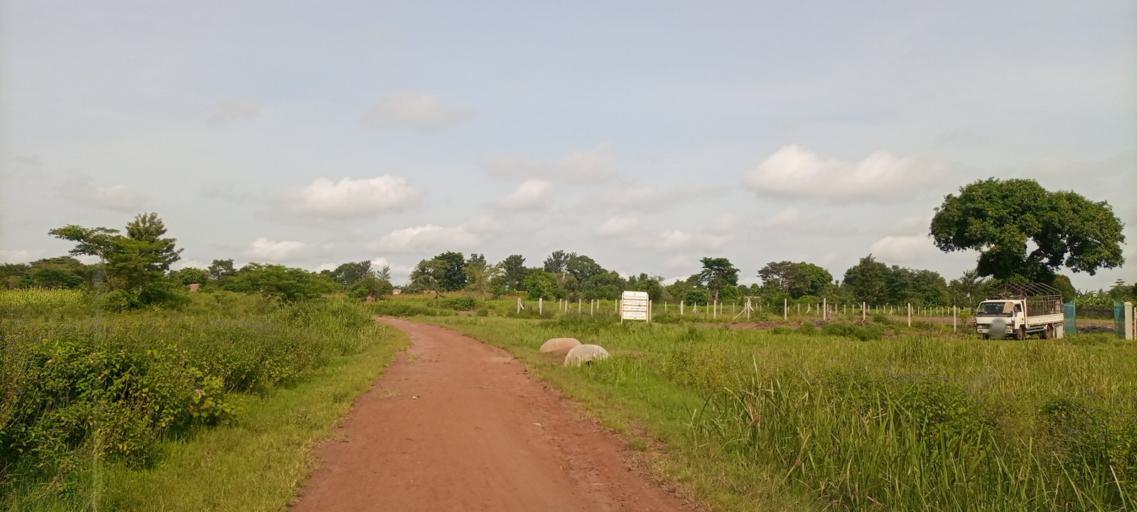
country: UG
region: Eastern Region
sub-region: Kibuku District
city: Kibuku
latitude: 1.0962
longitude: 33.7683
